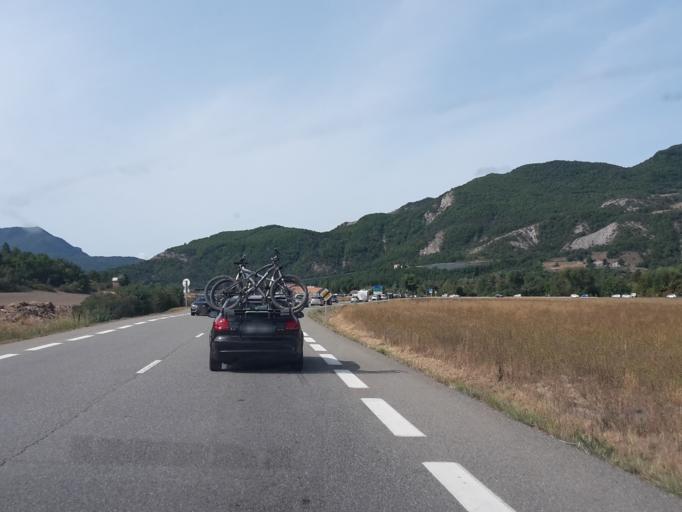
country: FR
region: Provence-Alpes-Cote d'Azur
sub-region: Departement des Hautes-Alpes
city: Tallard
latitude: 44.4499
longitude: 6.0369
